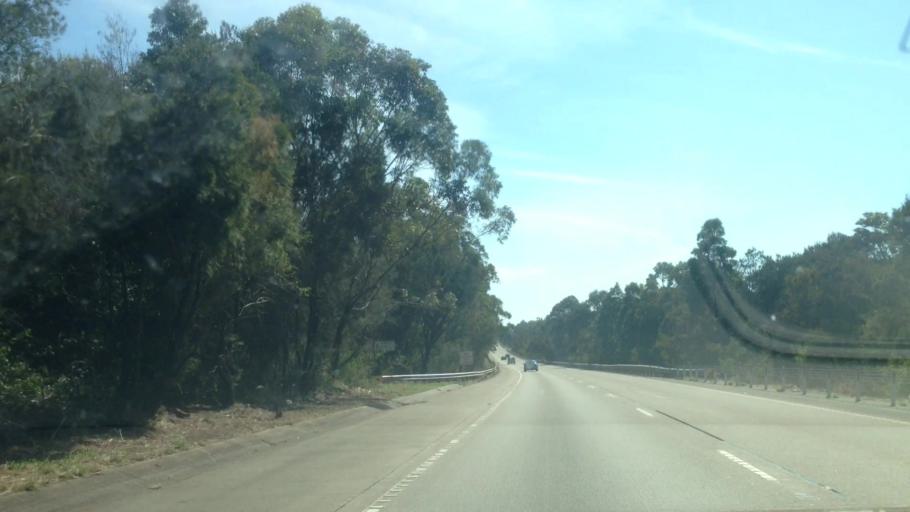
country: AU
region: New South Wales
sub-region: Lake Macquarie Shire
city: Fennell Bay
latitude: -32.9744
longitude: 151.5315
